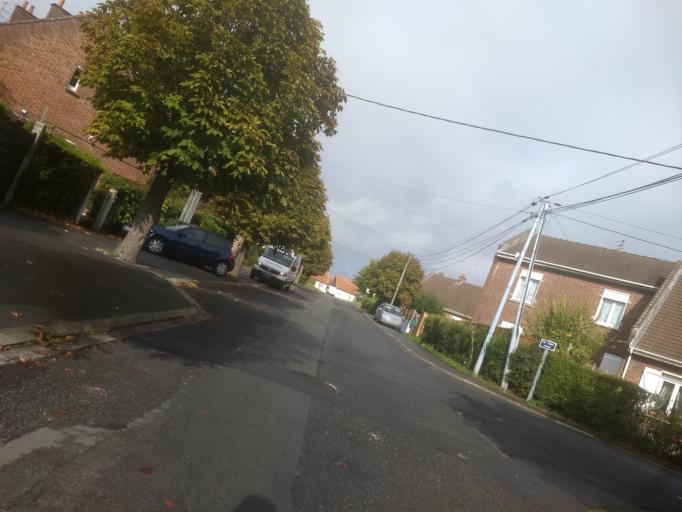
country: FR
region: Nord-Pas-de-Calais
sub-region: Departement du Pas-de-Calais
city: Arras
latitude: 50.2762
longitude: 2.7787
